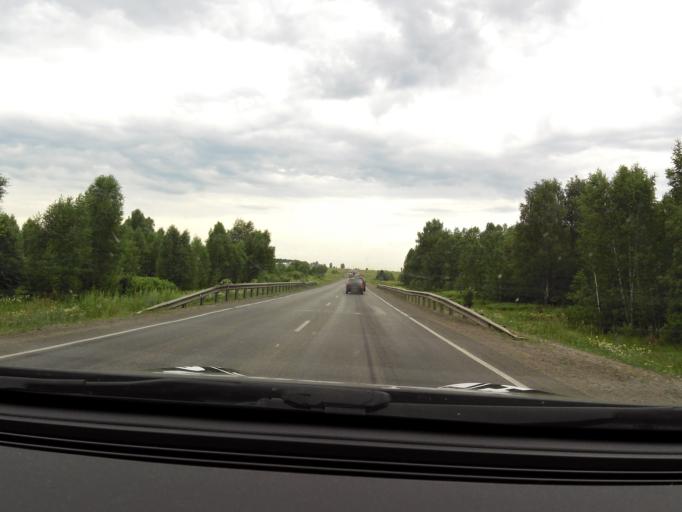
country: RU
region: Bashkortostan
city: Kudeyevskiy
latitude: 54.8171
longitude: 56.7779
